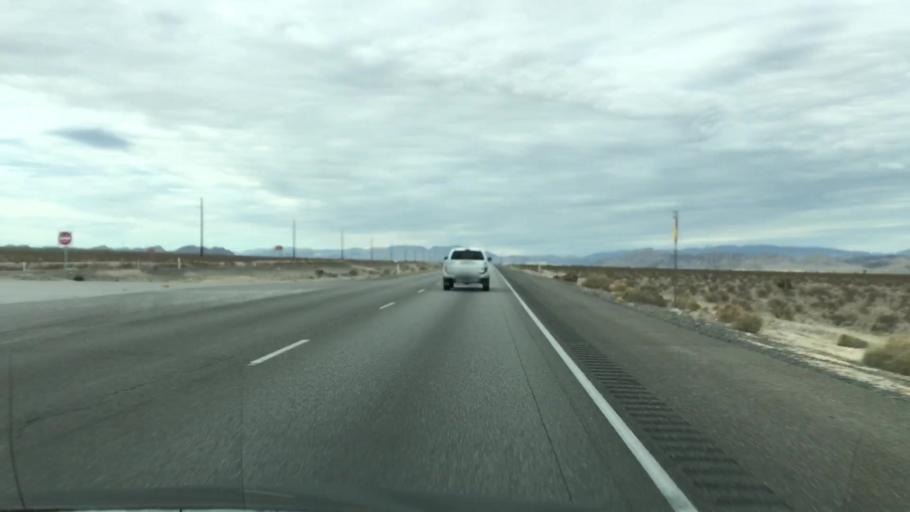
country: US
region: Nevada
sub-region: Clark County
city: Summerlin South
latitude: 36.5238
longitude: -115.5480
